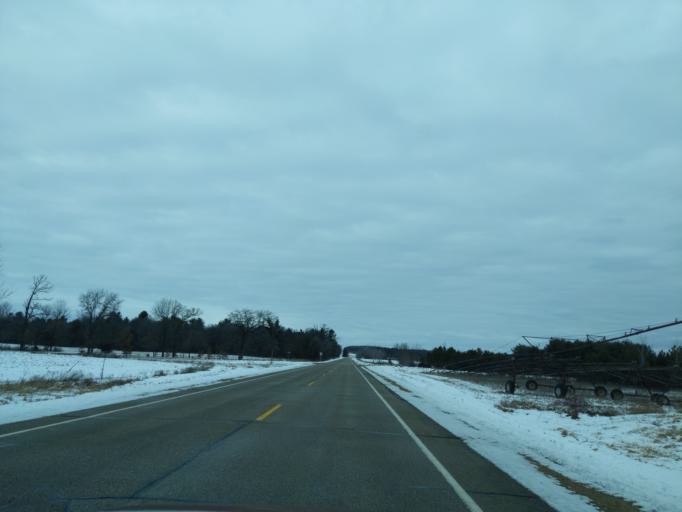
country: US
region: Wisconsin
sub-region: Waushara County
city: Wautoma
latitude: 43.9922
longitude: -89.3276
